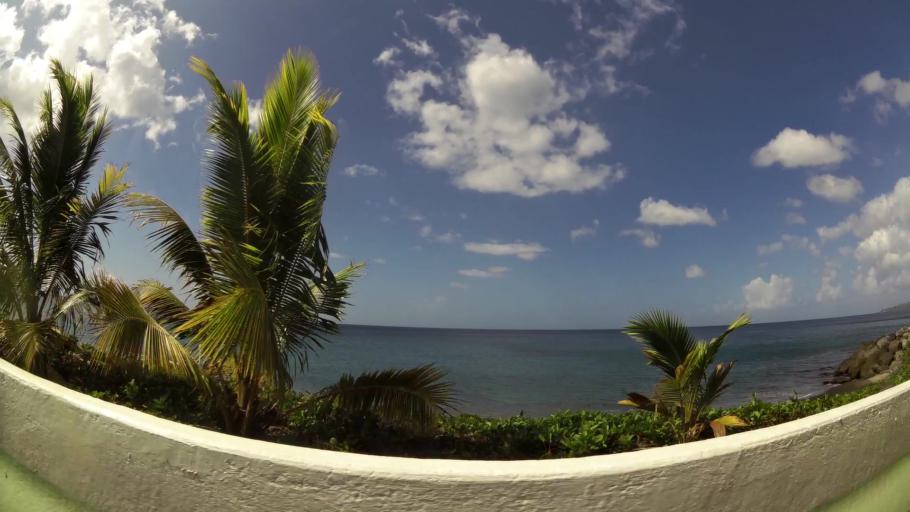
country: MQ
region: Martinique
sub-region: Martinique
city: Saint-Pierre
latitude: 14.7198
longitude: -61.1820
